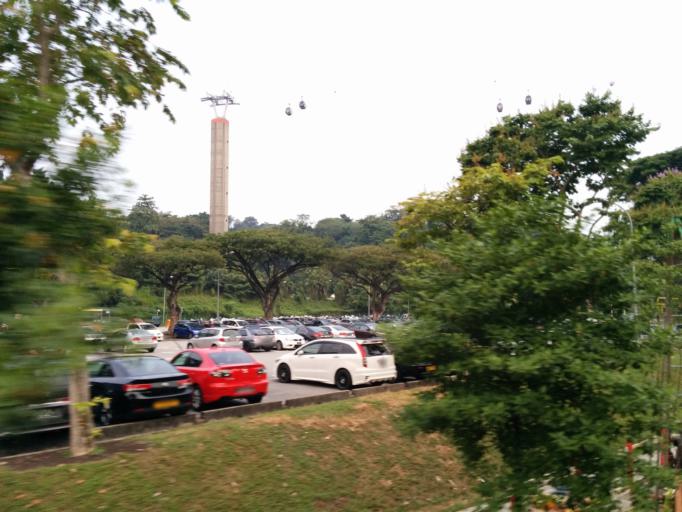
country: SG
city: Singapore
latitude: 1.2676
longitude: 103.8174
